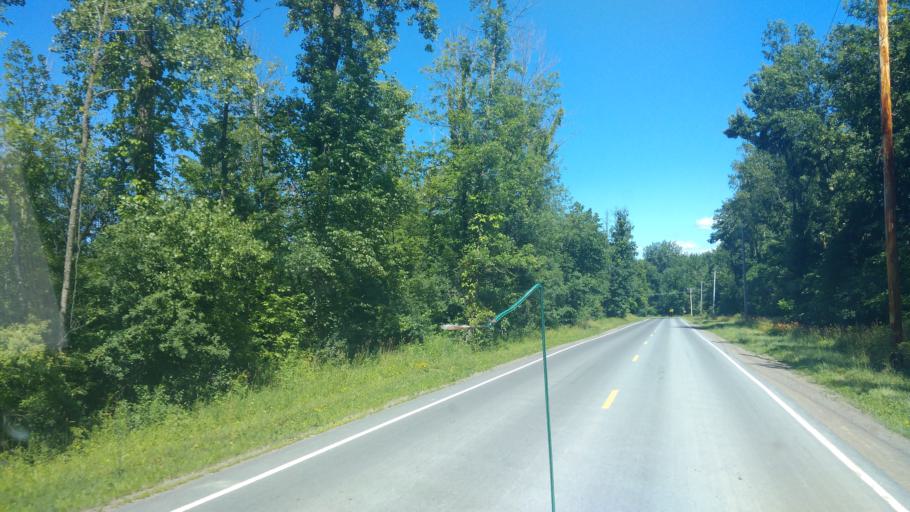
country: US
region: New York
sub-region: Wayne County
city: Sodus
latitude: 43.1802
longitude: -77.0146
